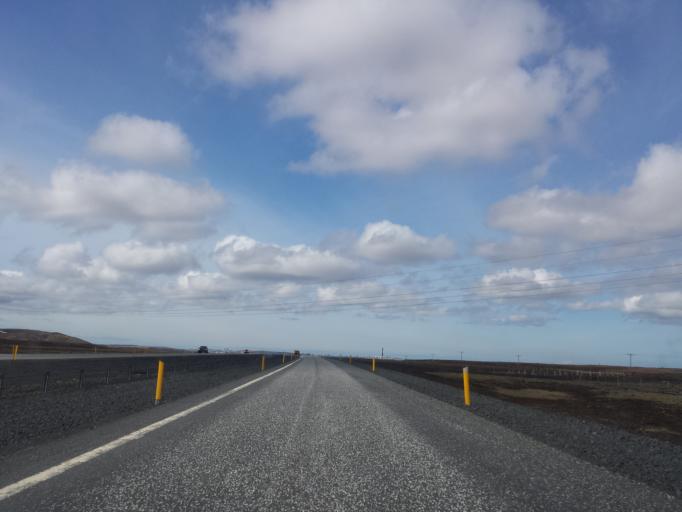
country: IS
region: Capital Region
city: Mosfellsbaer
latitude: 64.0702
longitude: -21.6066
